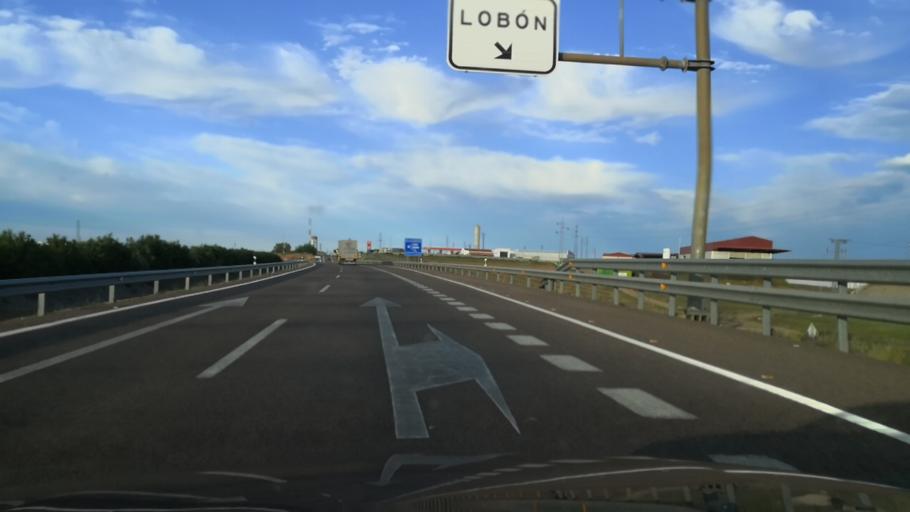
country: ES
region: Extremadura
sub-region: Provincia de Badajoz
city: Lobon
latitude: 38.8400
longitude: -6.6249
